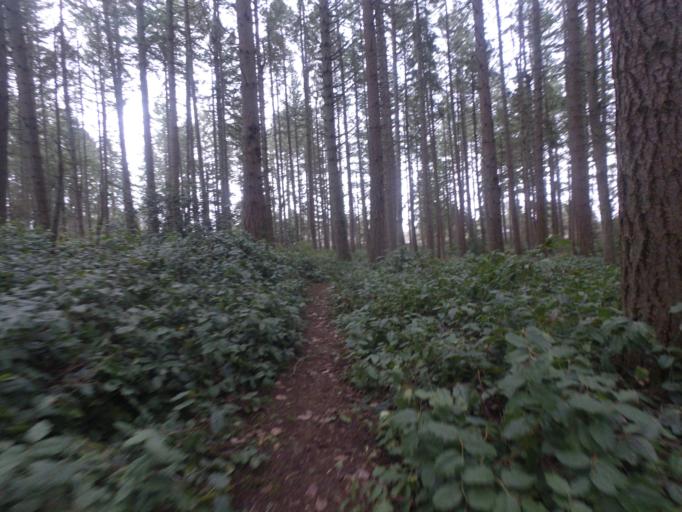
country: US
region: Washington
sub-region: Pierce County
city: University Place
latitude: 47.2089
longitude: -122.5519
